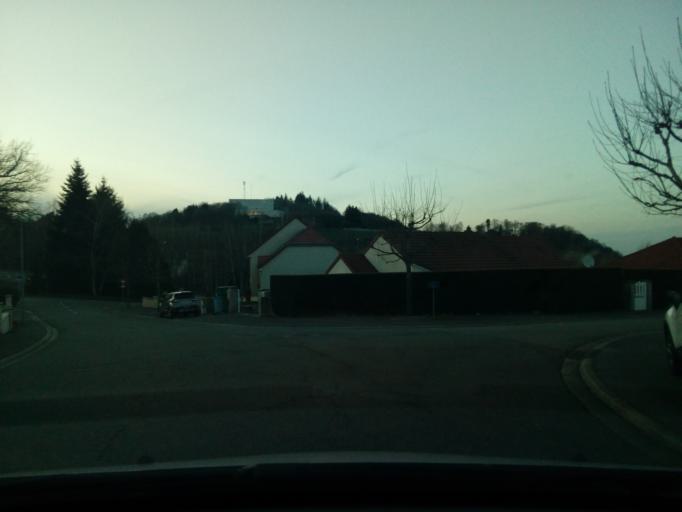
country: FR
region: Limousin
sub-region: Departement de la Creuse
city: Gueret
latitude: 46.1567
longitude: 1.8719
